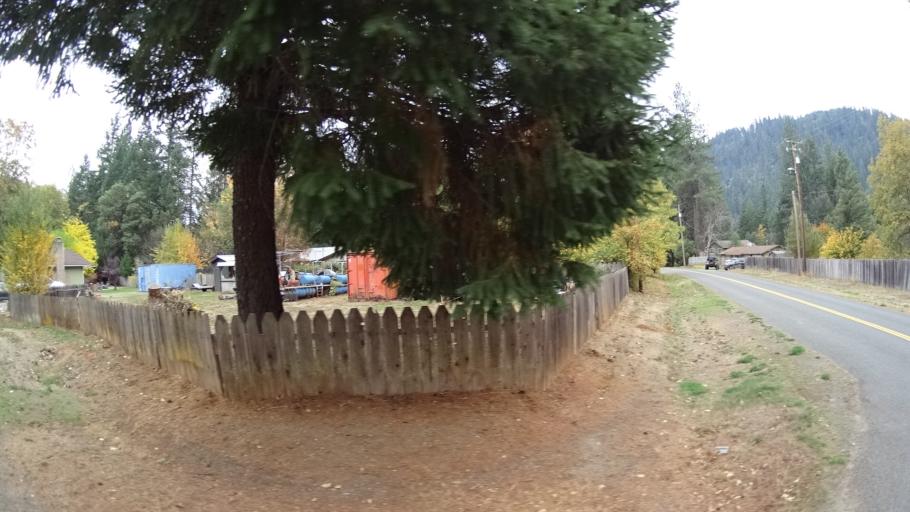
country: US
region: California
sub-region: Siskiyou County
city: Happy Camp
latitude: 41.8077
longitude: -123.3831
